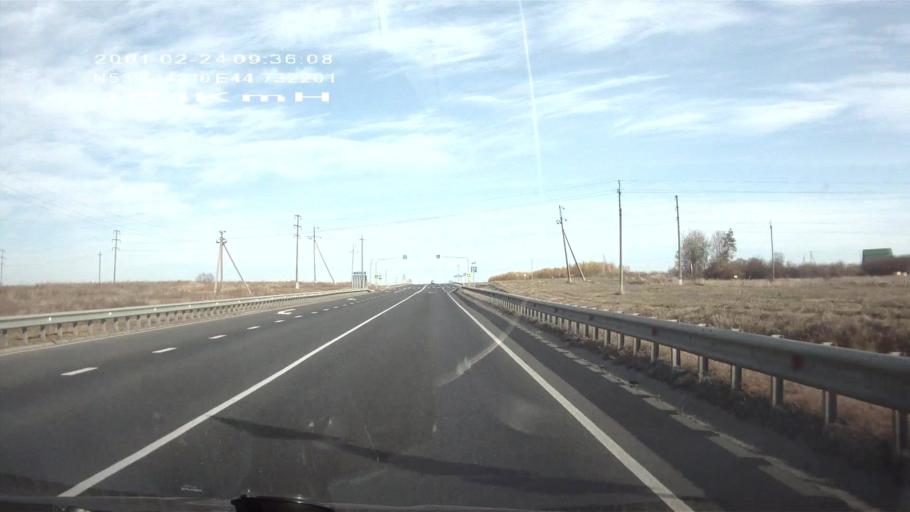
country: RU
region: Penza
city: Mokshan
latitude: 53.6144
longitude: 44.7323
